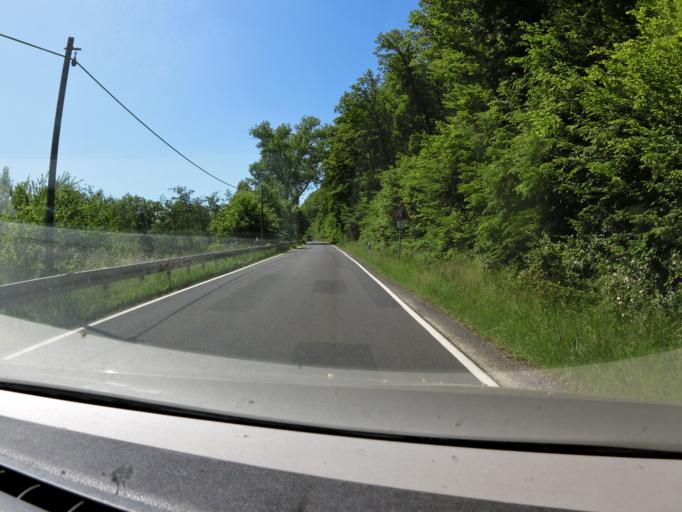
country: DE
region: Thuringia
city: Dorndorf
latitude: 50.8424
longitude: 10.0740
